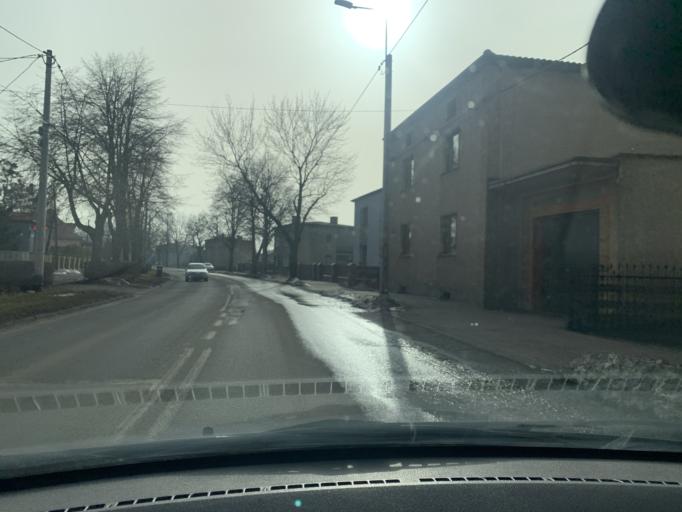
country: PL
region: Silesian Voivodeship
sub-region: Powiat tarnogorski
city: Radzionkow
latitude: 50.3927
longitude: 18.8978
